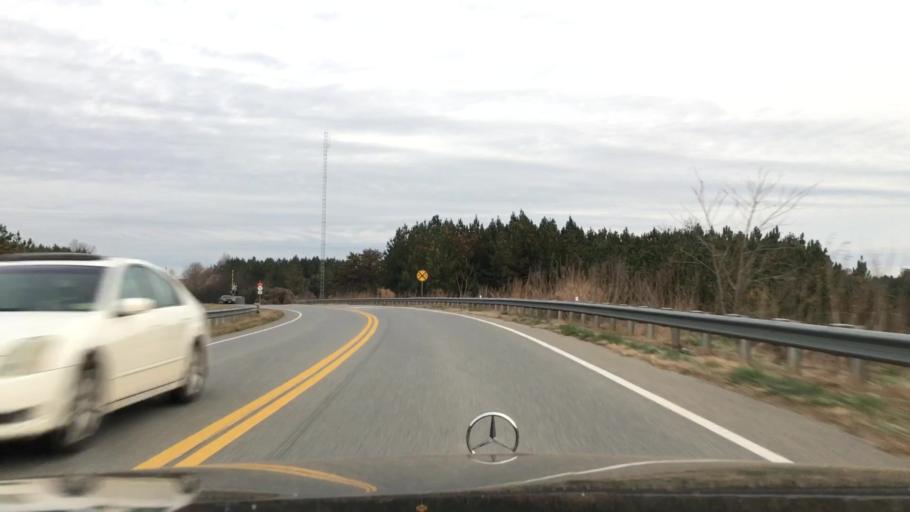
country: US
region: Virginia
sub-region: Campbell County
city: Altavista
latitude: 37.1924
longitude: -79.2943
